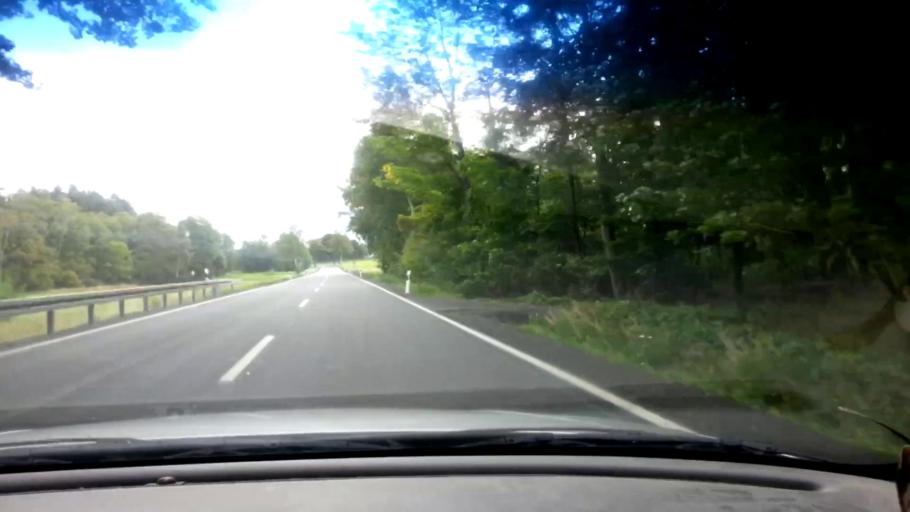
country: DE
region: Bavaria
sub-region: Upper Franconia
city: Wunsiedel
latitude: 50.0746
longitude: 12.0363
